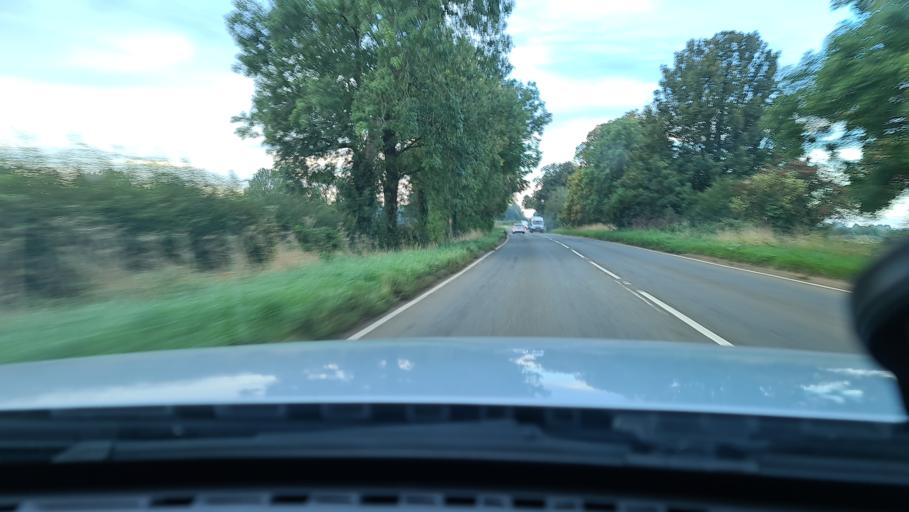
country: GB
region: England
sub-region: Oxfordshire
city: Hanwell
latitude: 52.0870
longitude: -1.3729
